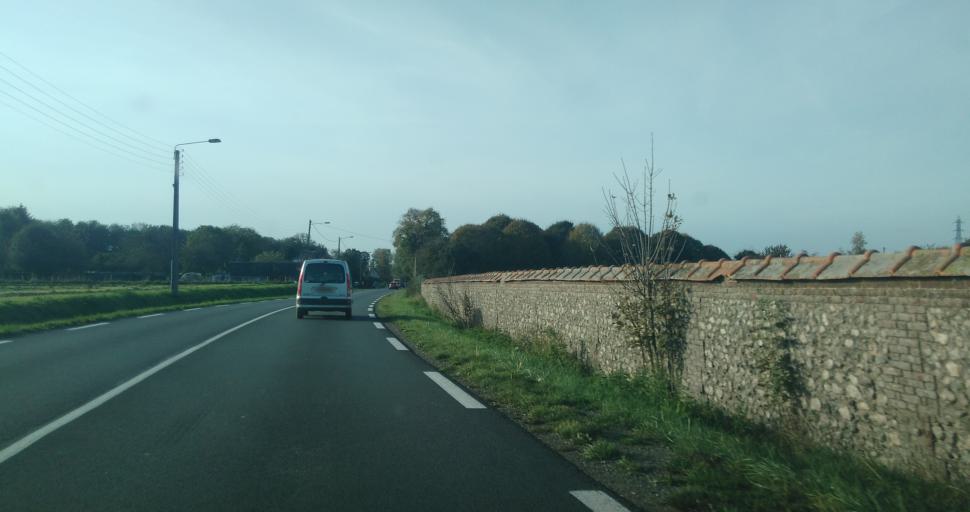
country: FR
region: Haute-Normandie
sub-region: Departement de l'Eure
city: Caumont
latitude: 49.3542
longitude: 0.9020
